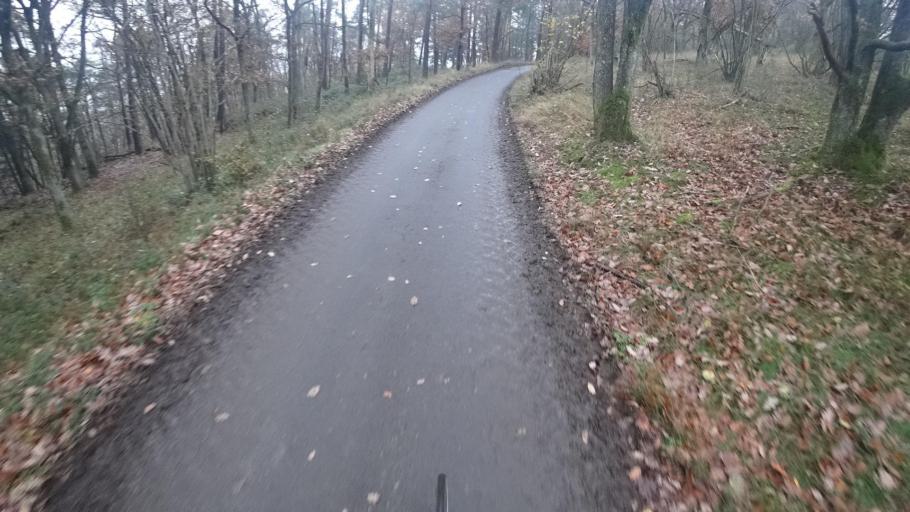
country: DE
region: Rheinland-Pfalz
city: Kesseling
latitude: 50.4961
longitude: 7.0127
